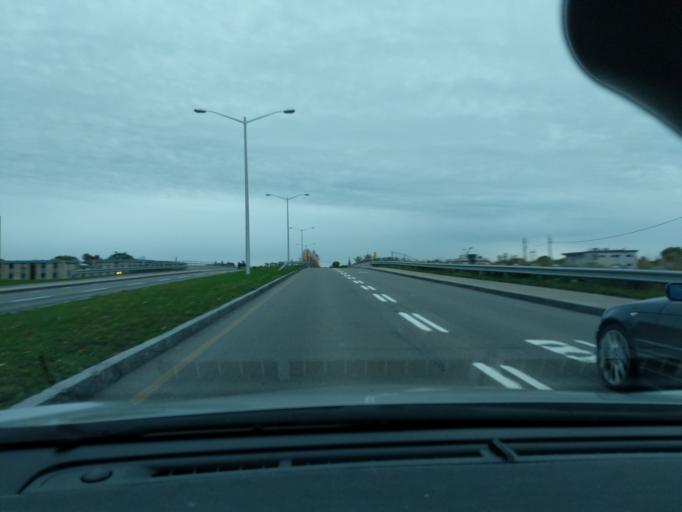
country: CA
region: Quebec
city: L'Ancienne-Lorette
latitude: 46.7661
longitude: -71.3123
